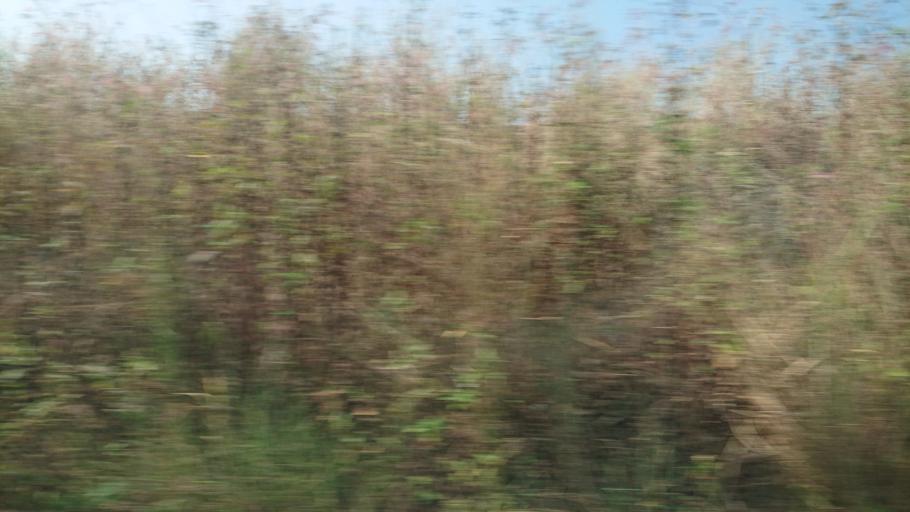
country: TW
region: Taiwan
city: Lugu
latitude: 23.7352
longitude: 120.6587
